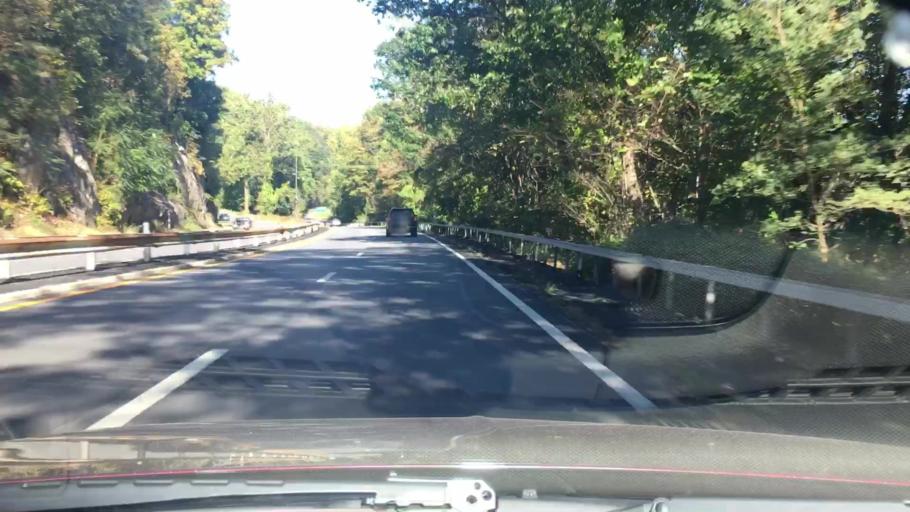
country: US
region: New York
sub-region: Westchester County
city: Chappaqua
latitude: 41.1653
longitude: -73.7701
